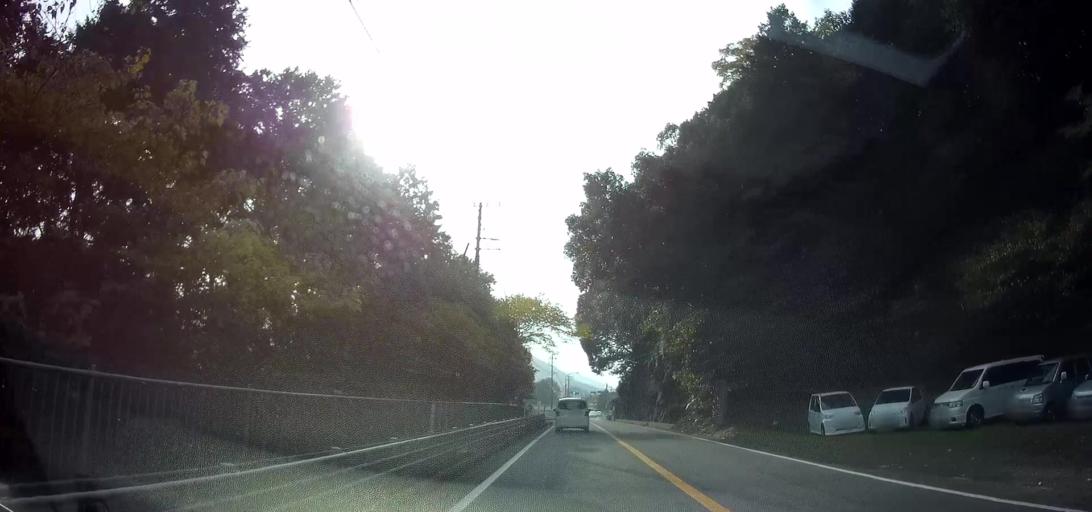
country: JP
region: Nagasaki
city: Shimabara
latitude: 32.7728
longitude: 130.2139
